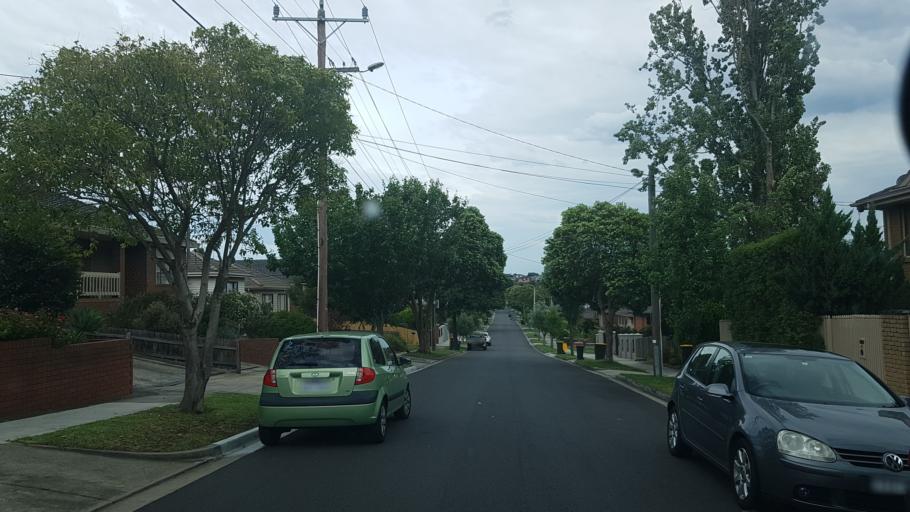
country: AU
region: Victoria
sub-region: Manningham
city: Bulleen
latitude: -37.7604
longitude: 145.0873
